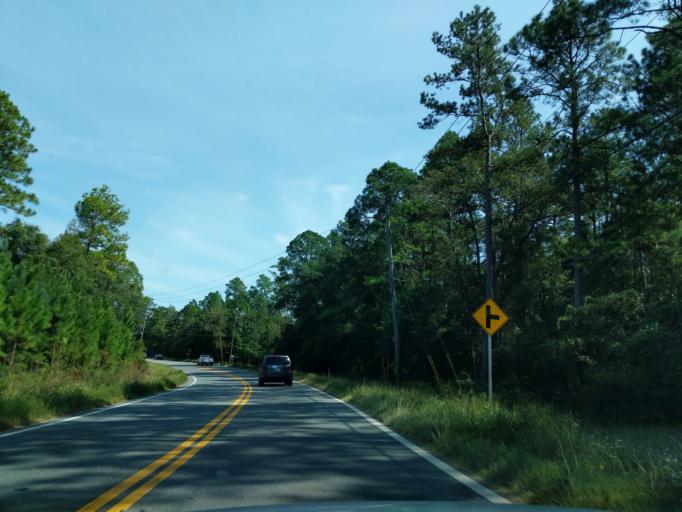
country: US
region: Florida
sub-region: Okaloosa County
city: Crestview
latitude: 30.7124
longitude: -86.6029
